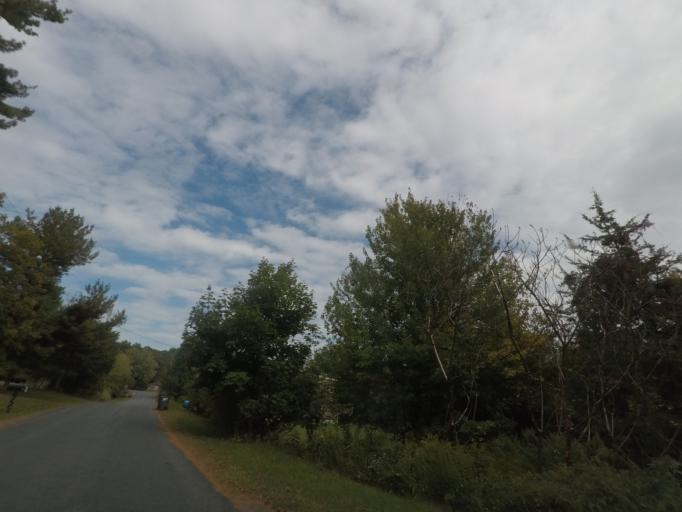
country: US
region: New York
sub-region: Rensselaer County
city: Nassau
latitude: 42.5401
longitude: -73.6662
